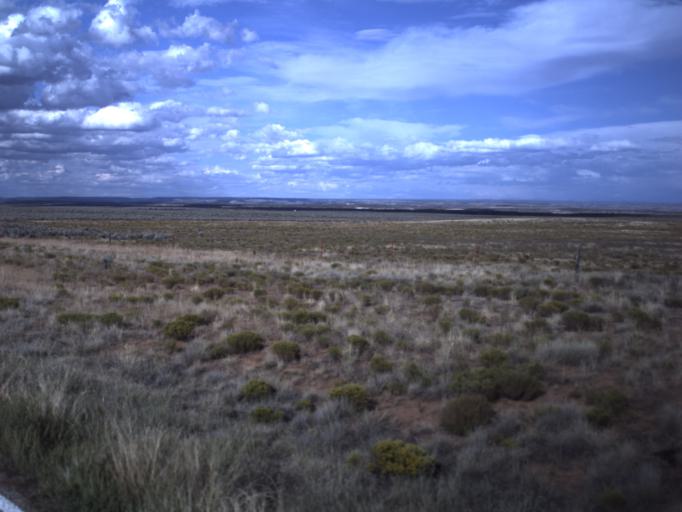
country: US
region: Utah
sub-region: San Juan County
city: Blanding
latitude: 37.3761
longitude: -109.3423
